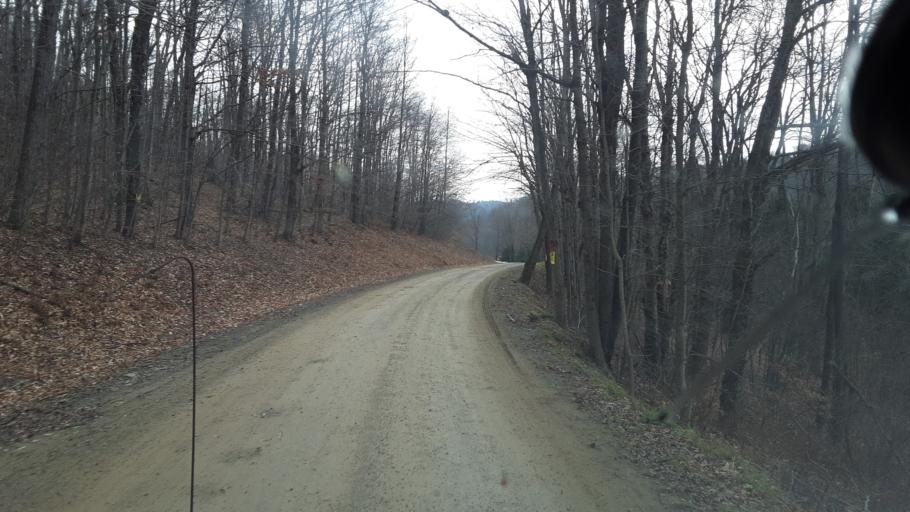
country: US
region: Pennsylvania
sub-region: Tioga County
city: Westfield
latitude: 41.9099
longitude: -77.7182
